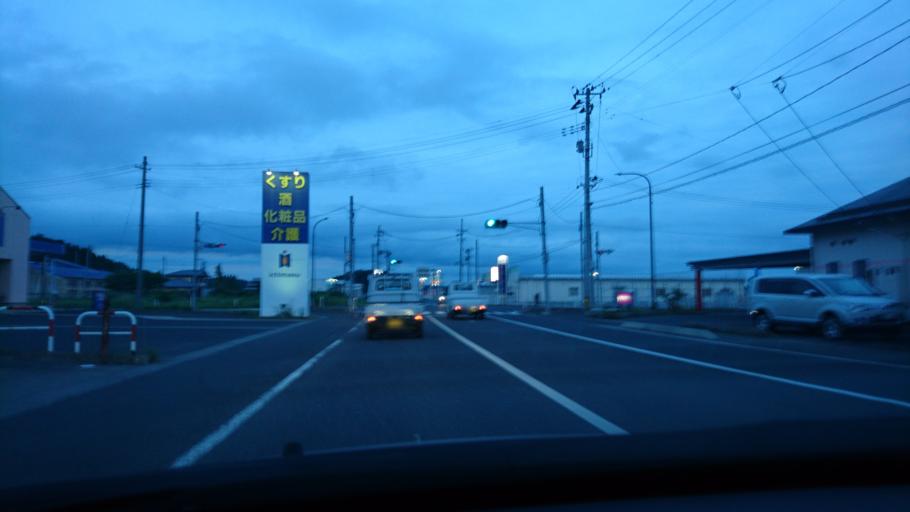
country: JP
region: Iwate
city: Ichinoseki
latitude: 38.8317
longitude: 140.9986
